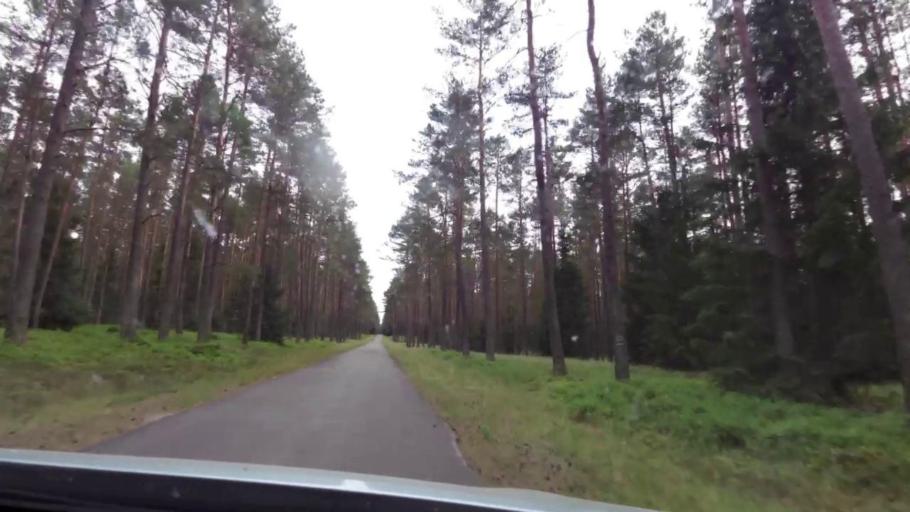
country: PL
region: Pomeranian Voivodeship
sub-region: Powiat bytowski
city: Trzebielino
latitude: 54.2193
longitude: 17.0030
